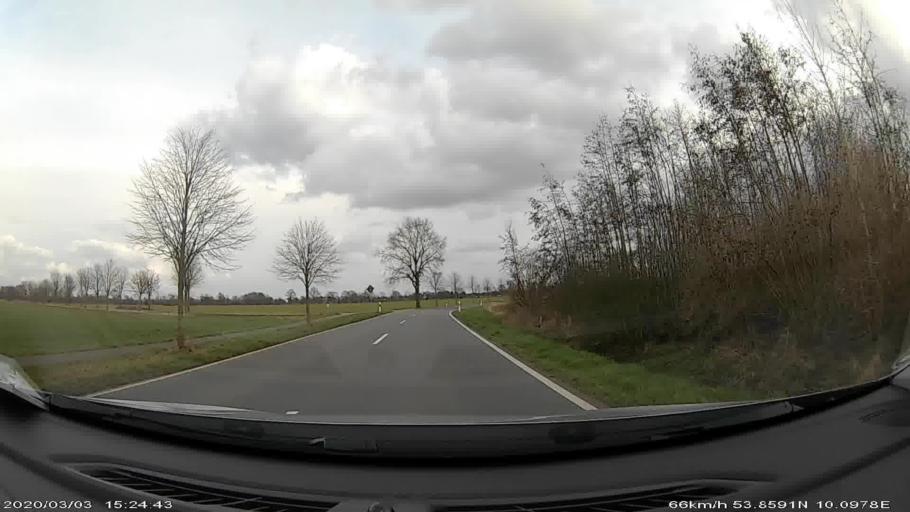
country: DE
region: Schleswig-Holstein
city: Sievershutten
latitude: 53.8591
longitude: 10.0970
